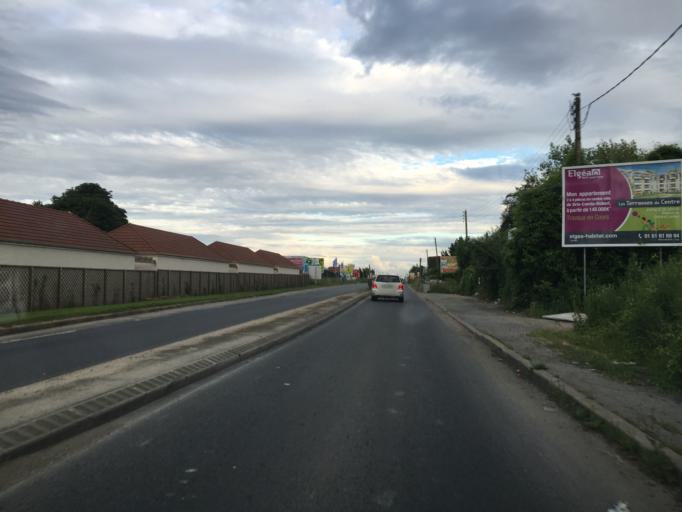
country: FR
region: Ile-de-France
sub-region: Departement du Val-de-Marne
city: Santeny
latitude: 48.7151
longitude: 2.5747
